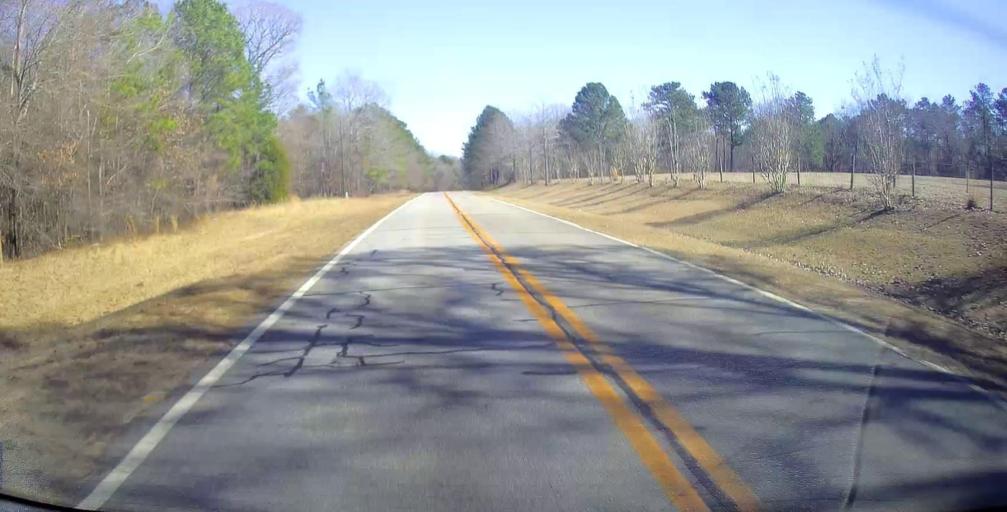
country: US
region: Georgia
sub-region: Peach County
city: Byron
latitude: 32.6111
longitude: -83.8109
